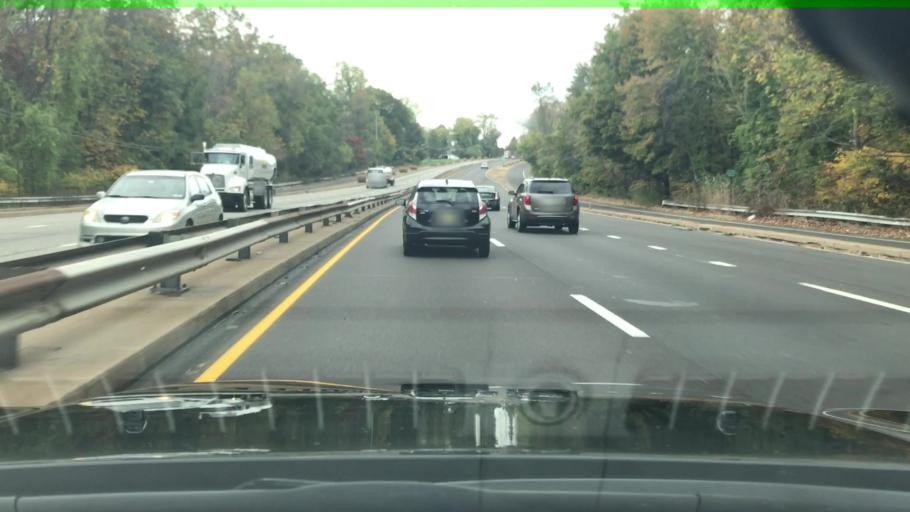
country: US
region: Pennsylvania
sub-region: Bucks County
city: Langhorne Manor
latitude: 40.1660
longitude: -74.9248
